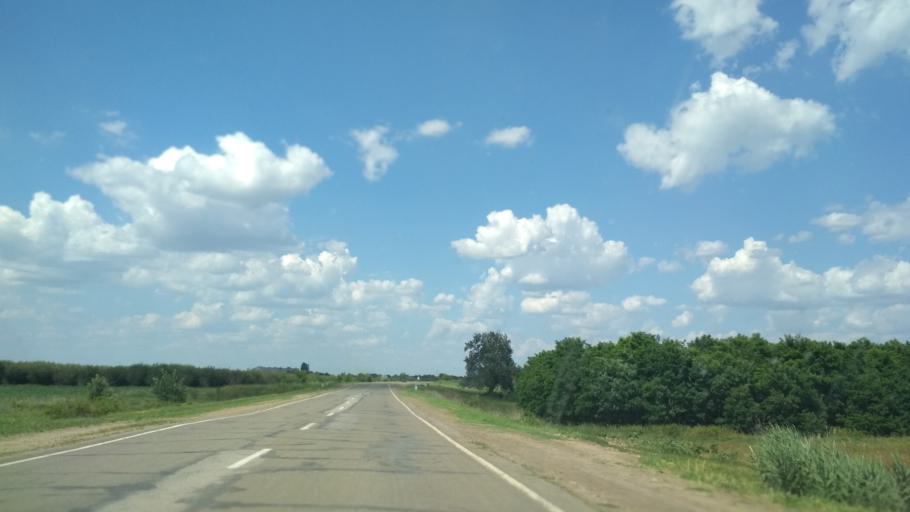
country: MD
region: Chisinau
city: Vadul lui Voda
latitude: 47.1100
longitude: 29.1027
